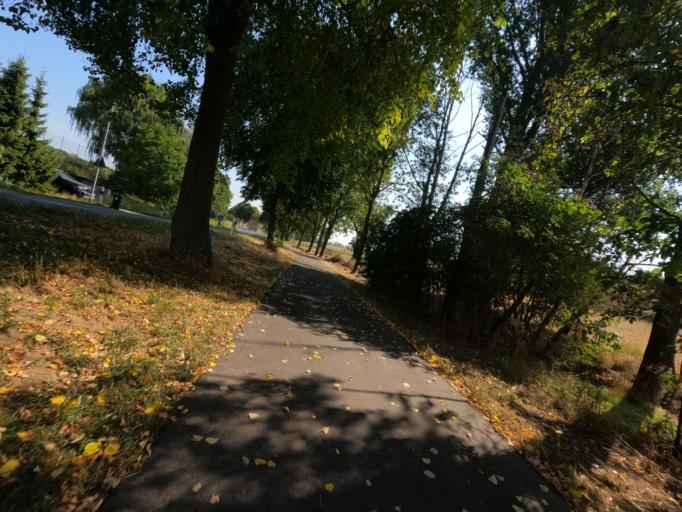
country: DE
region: North Rhine-Westphalia
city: Julich
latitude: 50.9727
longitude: 6.3377
